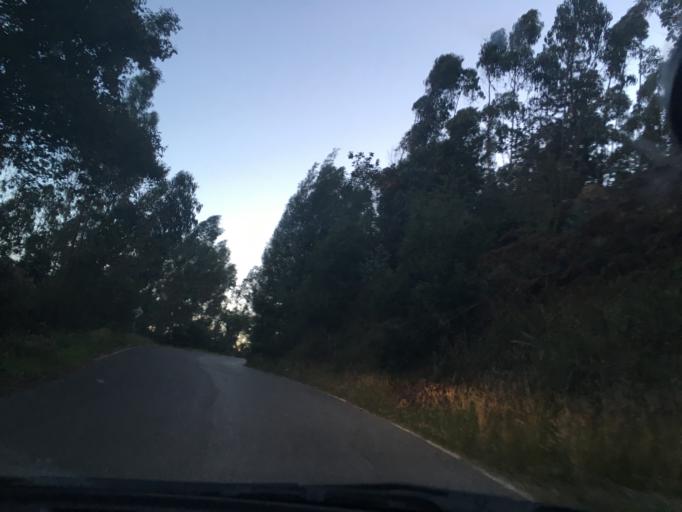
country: CO
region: Boyaca
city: Aquitania
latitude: 5.6122
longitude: -72.9088
